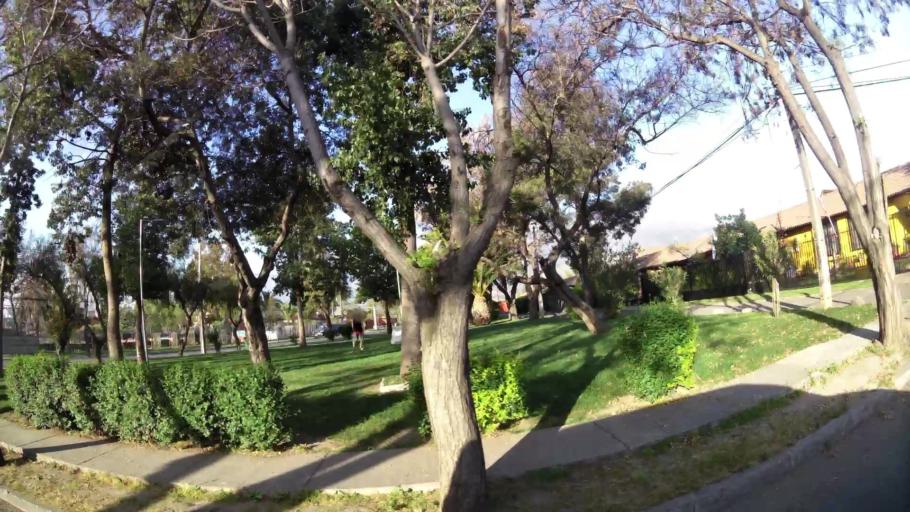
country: CL
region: Santiago Metropolitan
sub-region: Provincia de Santiago
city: La Pintana
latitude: -33.5439
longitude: -70.5792
